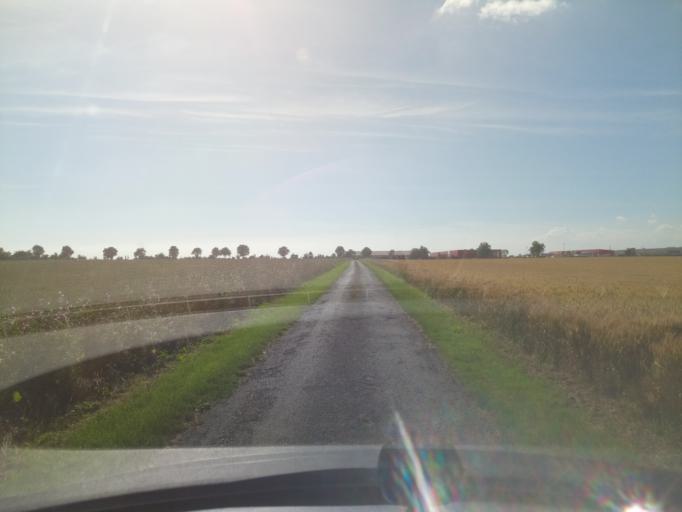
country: FR
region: Poitou-Charentes
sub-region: Departement de la Charente-Maritime
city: Andilly
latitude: 46.2577
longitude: -1.0063
